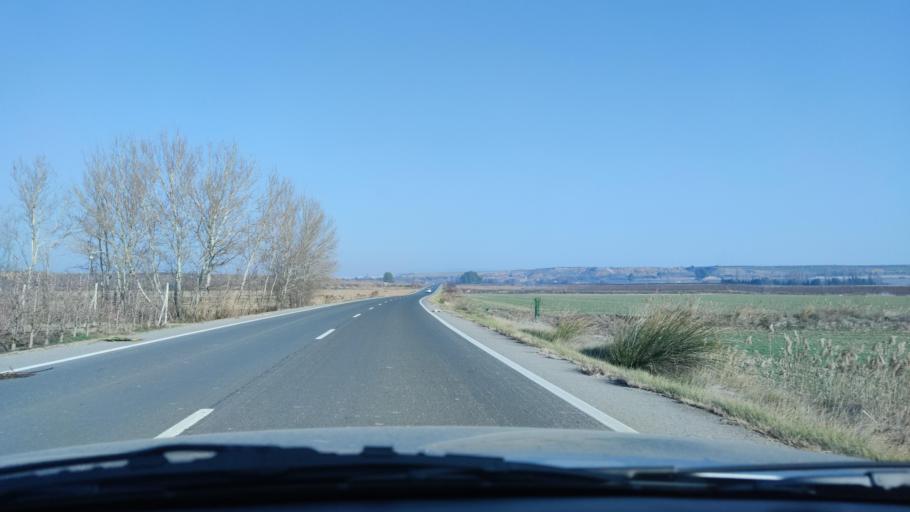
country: ES
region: Catalonia
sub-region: Provincia de Lleida
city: Albesa
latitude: 41.7156
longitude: 0.6393
